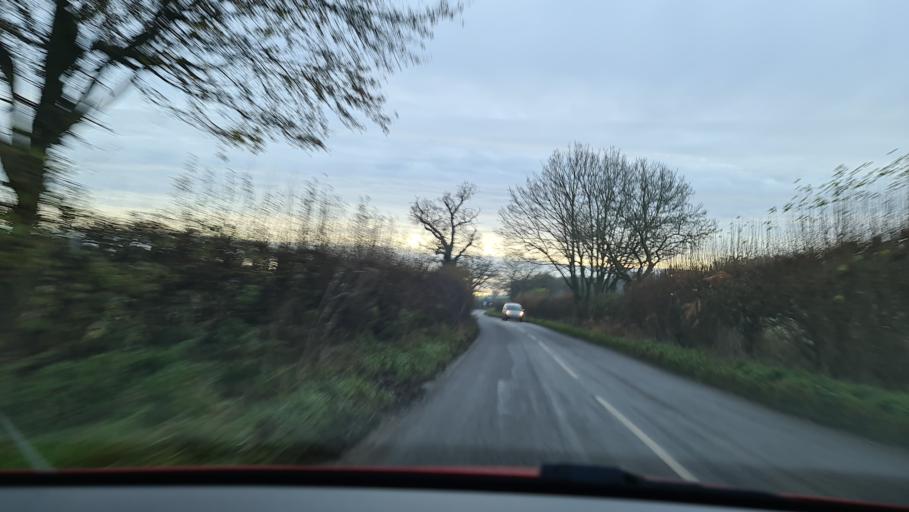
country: GB
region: England
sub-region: Buckinghamshire
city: Great Missenden
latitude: 51.7116
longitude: -0.7443
